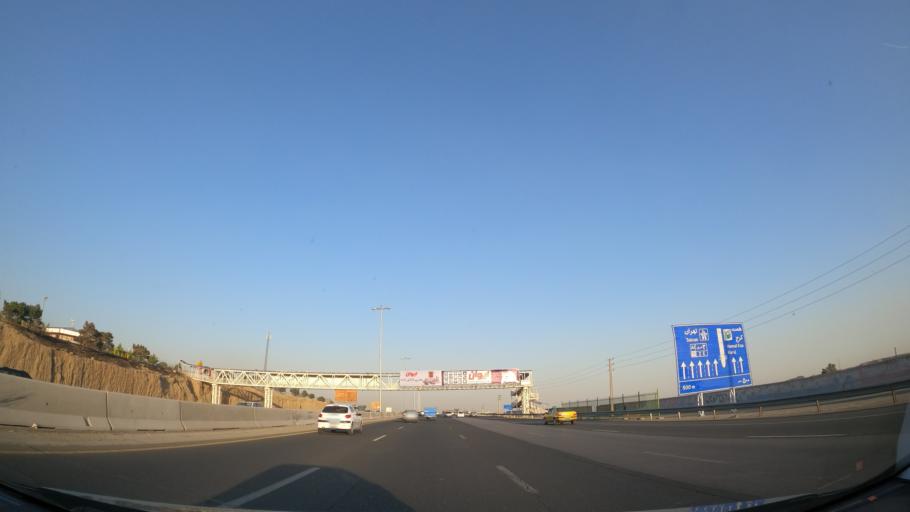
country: IR
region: Tehran
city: Shahr-e Qods
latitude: 35.7506
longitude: 51.0801
